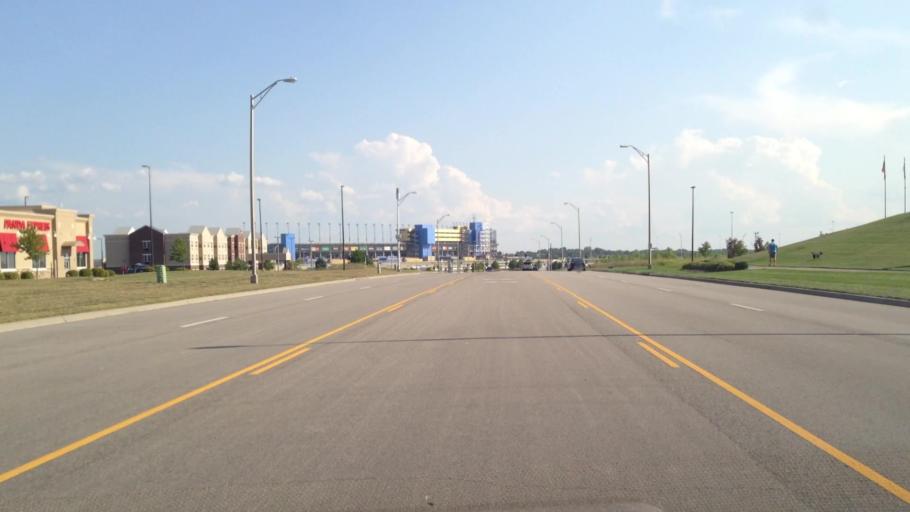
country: US
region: Kansas
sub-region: Wyandotte County
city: Edwardsville
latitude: 39.1322
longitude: -94.8332
